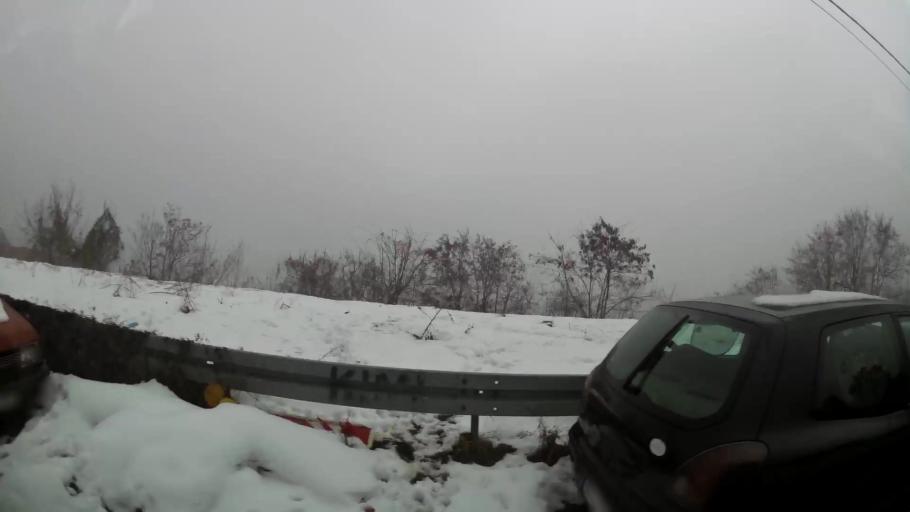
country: RS
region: Central Serbia
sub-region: Belgrade
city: Zvezdara
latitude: 44.7823
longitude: 20.5309
